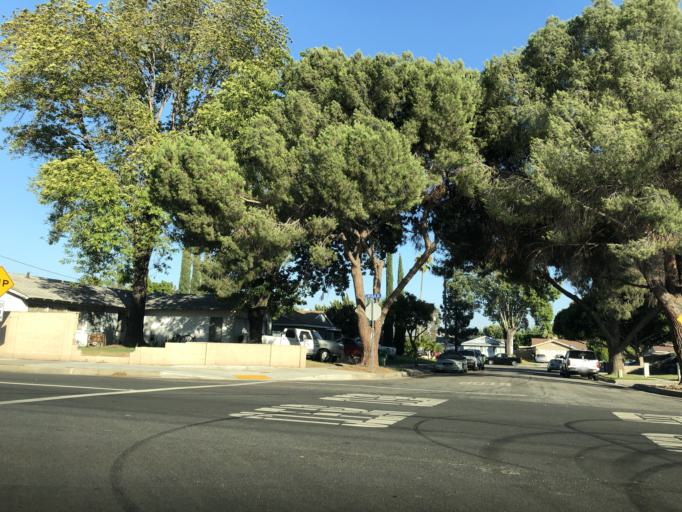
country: US
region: California
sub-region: Riverside County
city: Corona
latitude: 33.9009
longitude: -117.5725
